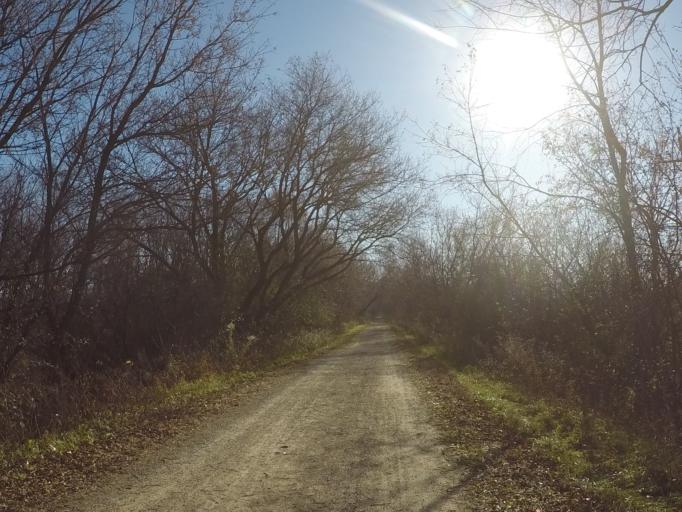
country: US
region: Wisconsin
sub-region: Dane County
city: Deerfield
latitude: 43.0505
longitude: -89.0631
